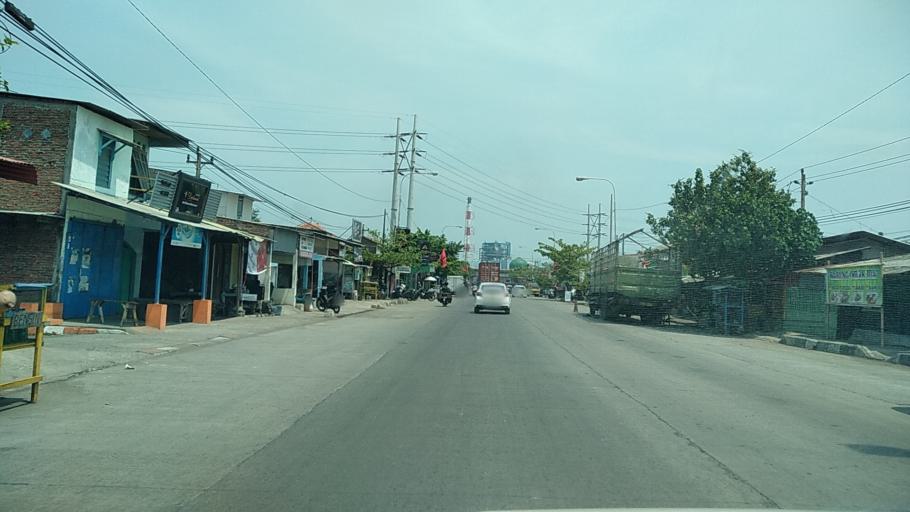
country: ID
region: Central Java
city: Semarang
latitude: -6.9573
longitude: 110.4307
